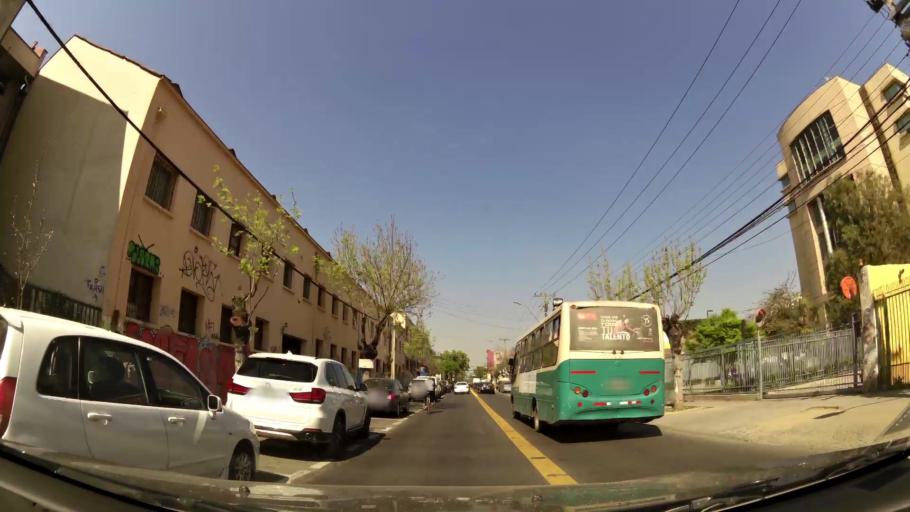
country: CL
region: Santiago Metropolitan
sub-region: Provincia de Maipo
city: San Bernardo
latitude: -33.5902
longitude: -70.7059
